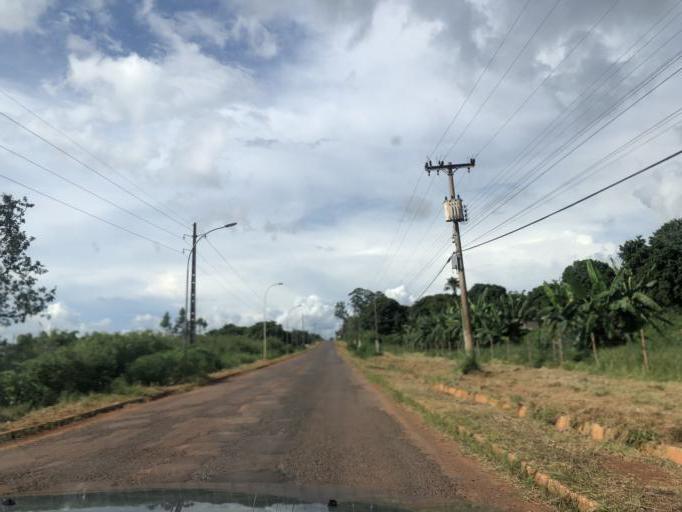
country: BR
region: Federal District
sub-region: Brasilia
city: Brasilia
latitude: -15.7428
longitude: -48.1255
